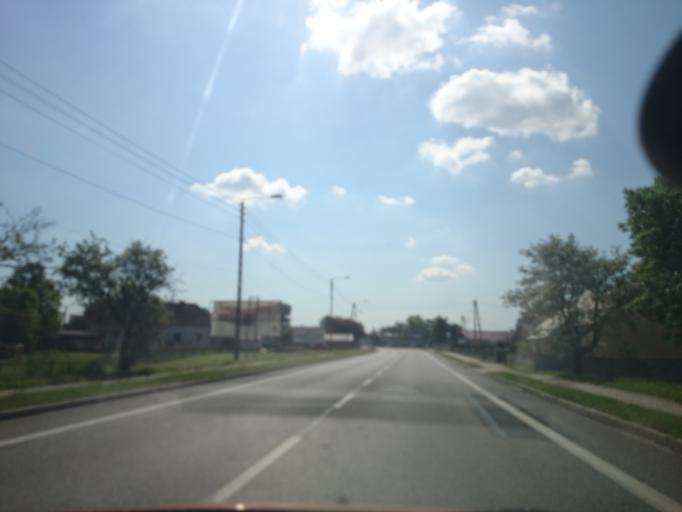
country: PL
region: Opole Voivodeship
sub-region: Powiat opolski
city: Naklo
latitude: 50.5815
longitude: 18.1121
